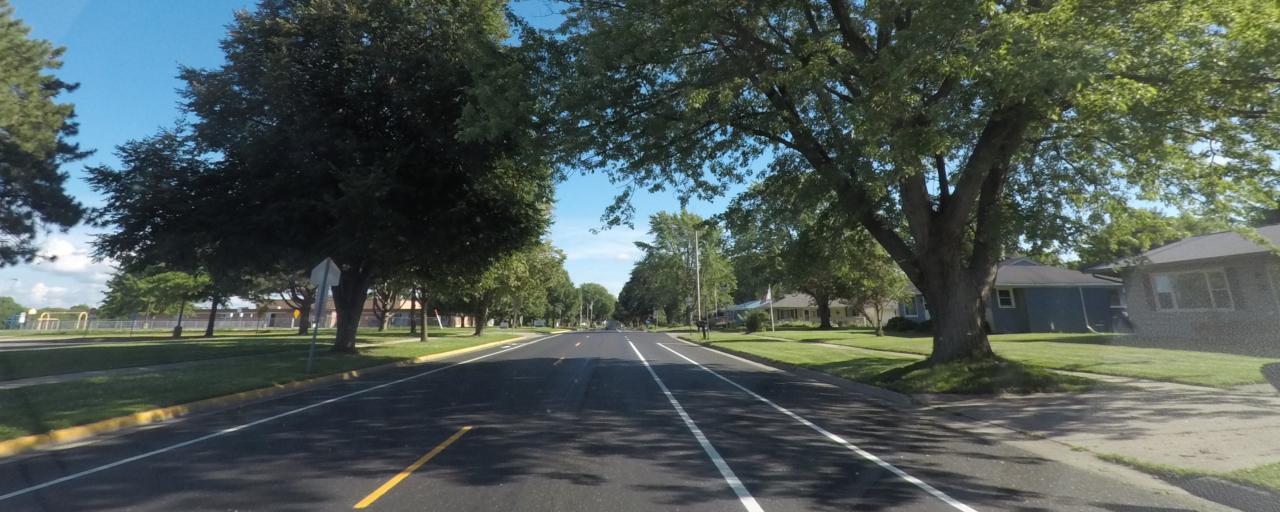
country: US
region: Wisconsin
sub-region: Rock County
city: Janesville
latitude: 42.6920
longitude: -88.9875
